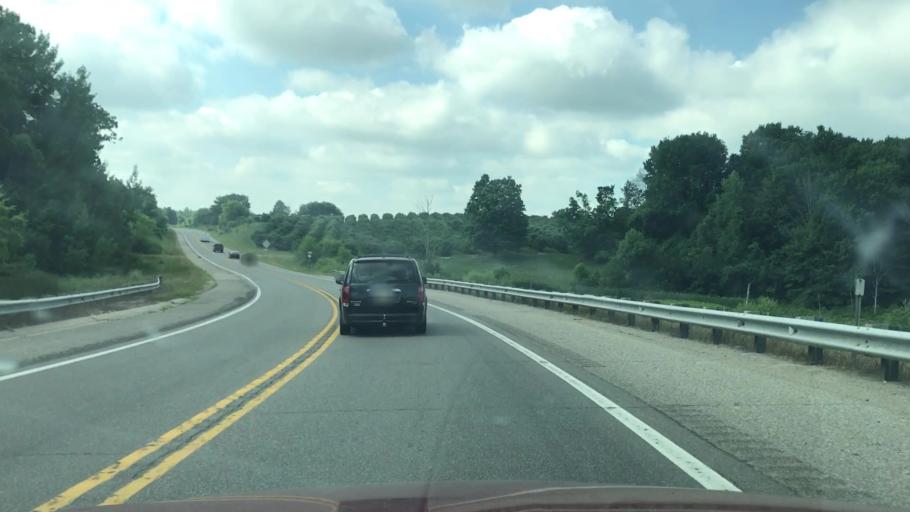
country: US
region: Michigan
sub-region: Kent County
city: Kent City
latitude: 43.2620
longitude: -85.8157
